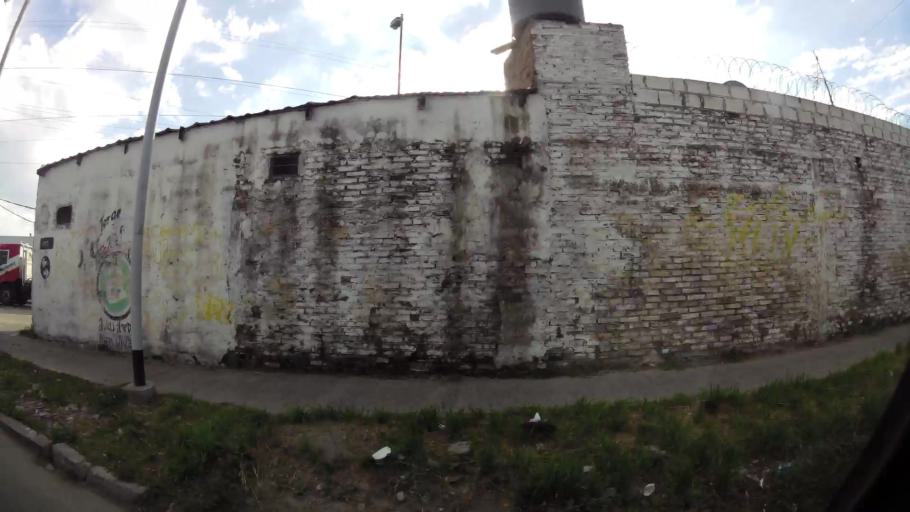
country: AR
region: Buenos Aires
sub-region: Partido de Lanus
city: Lanus
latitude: -34.7054
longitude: -58.3581
